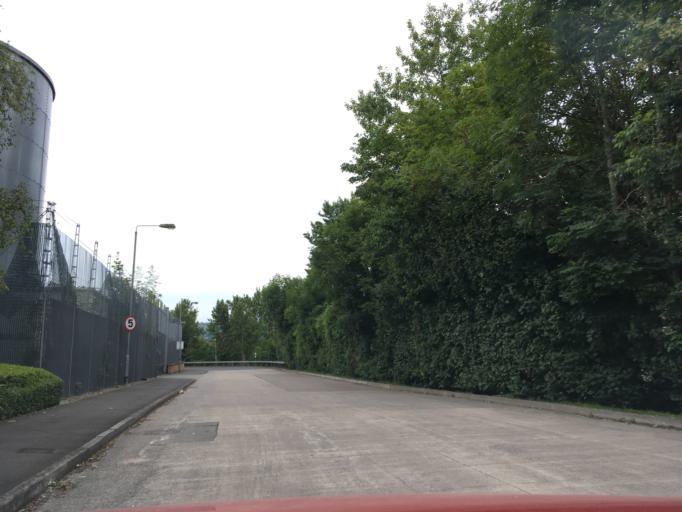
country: GB
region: England
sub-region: Bristol
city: Bristol
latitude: 51.4174
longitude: -2.6026
